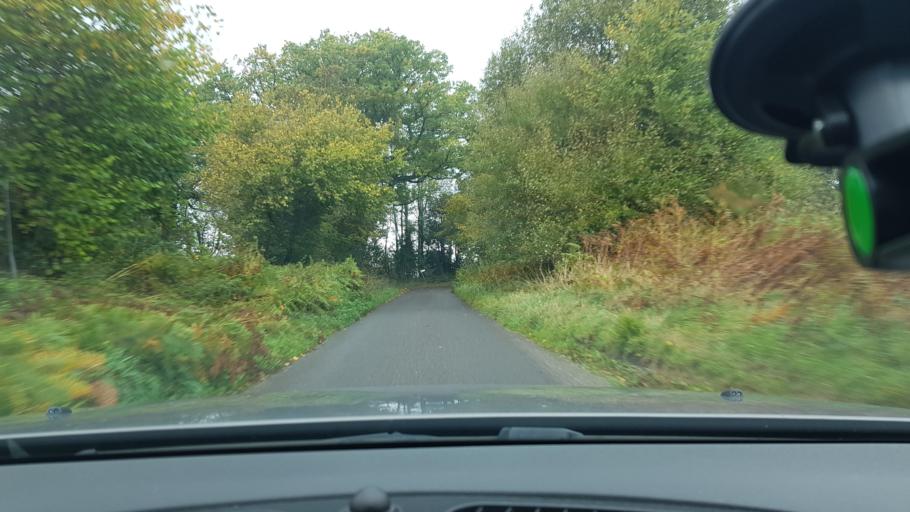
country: GB
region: England
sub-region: Wiltshire
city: Burbage
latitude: 51.3570
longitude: -1.7044
